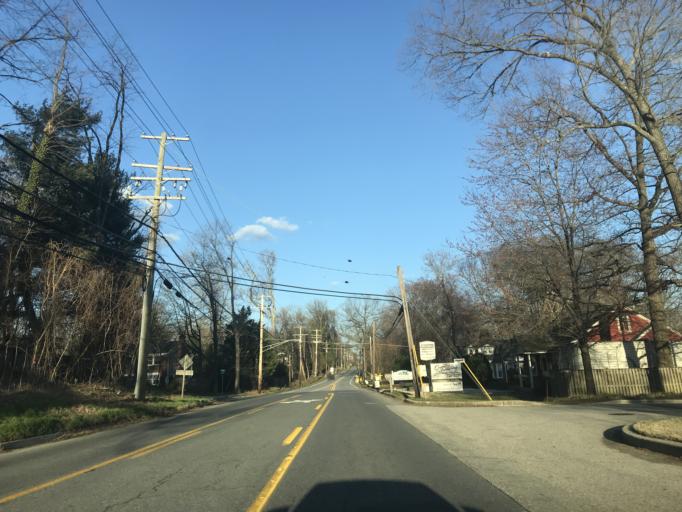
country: US
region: Maryland
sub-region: Anne Arundel County
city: Crofton
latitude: 38.9920
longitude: -76.6942
